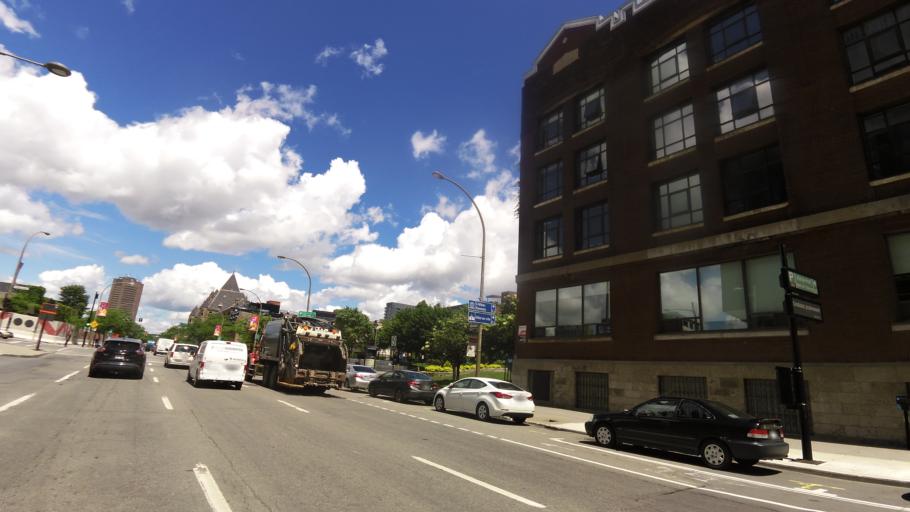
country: CA
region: Quebec
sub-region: Montreal
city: Montreal
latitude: 45.5105
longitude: -73.5548
